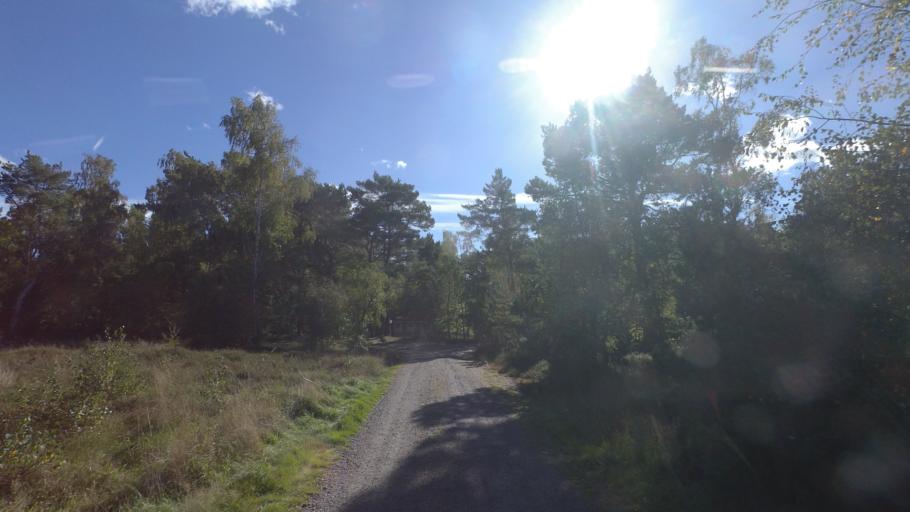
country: DK
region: Capital Region
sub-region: Bornholm Kommune
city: Nexo
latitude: 55.0010
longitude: 15.0893
